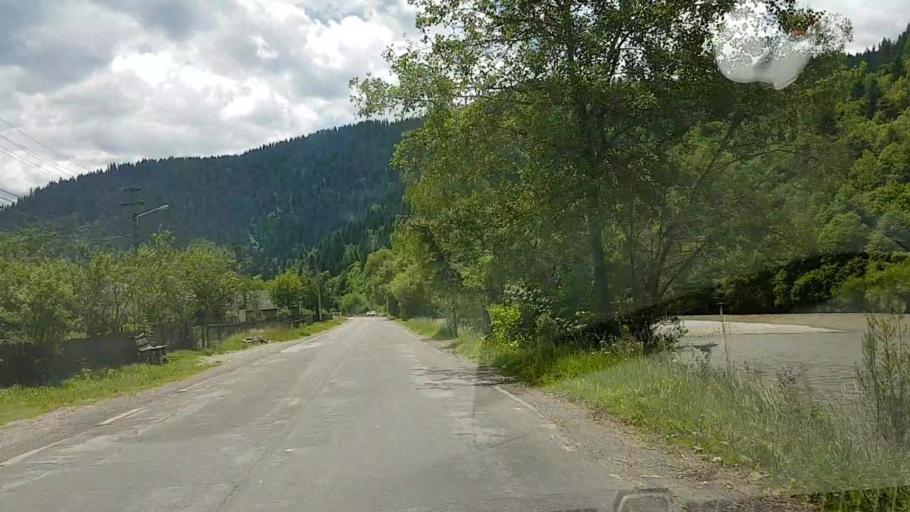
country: RO
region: Suceava
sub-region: Comuna Brosteni
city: Brosteni
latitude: 47.2496
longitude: 25.6933
